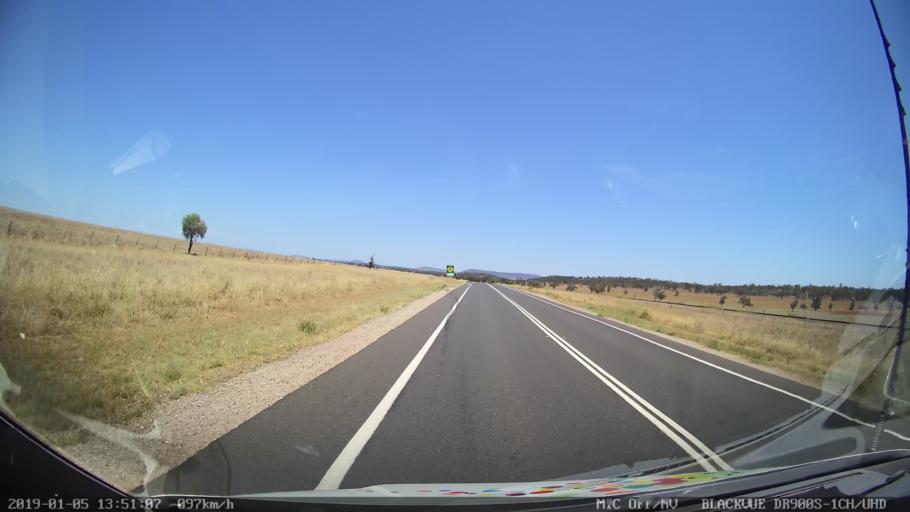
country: AU
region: New South Wales
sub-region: Gunnedah
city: Gunnedah
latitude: -31.0400
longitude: 150.2764
